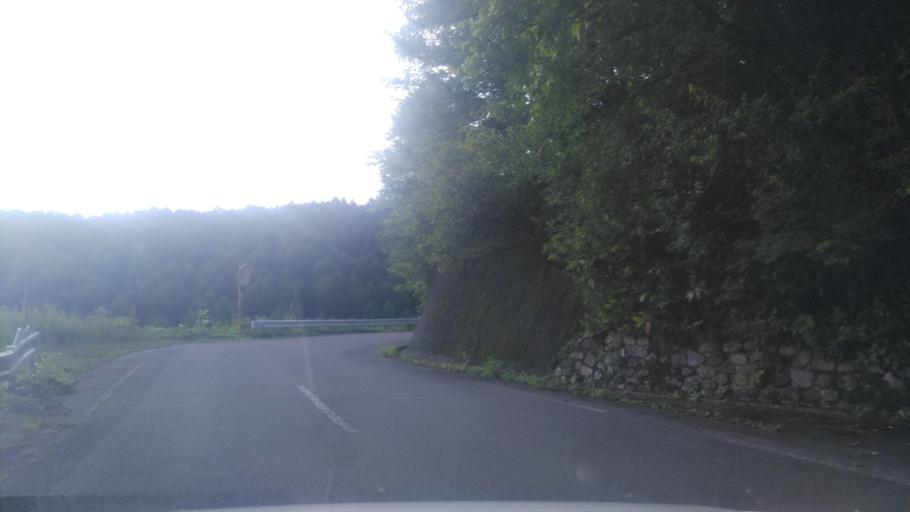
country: JP
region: Nagano
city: Ueda
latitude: 36.5135
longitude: 138.3661
